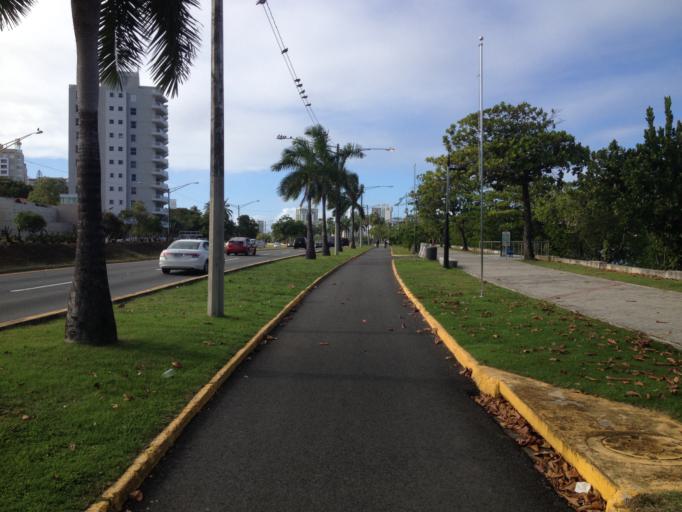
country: PR
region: San Juan
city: San Juan
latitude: 18.4551
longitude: -66.0780
